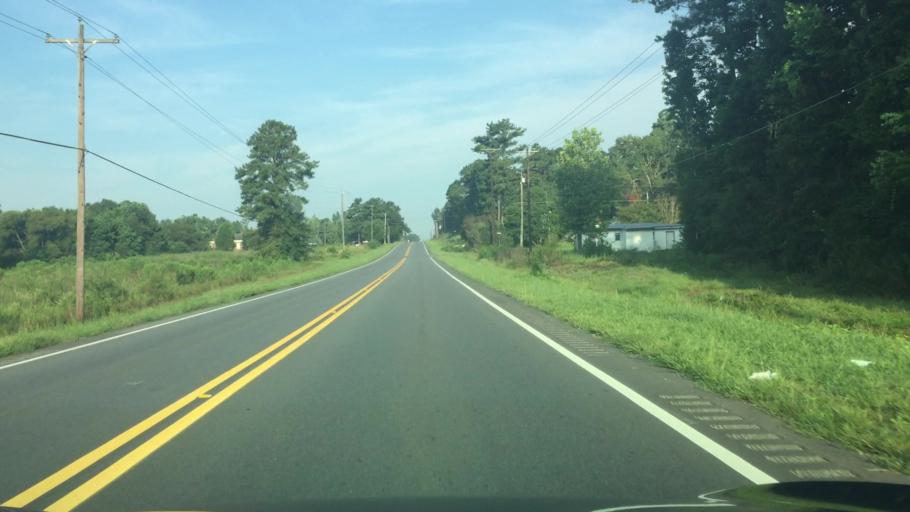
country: US
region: Alabama
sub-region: Covington County
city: Andalusia
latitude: 31.2782
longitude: -86.4853
